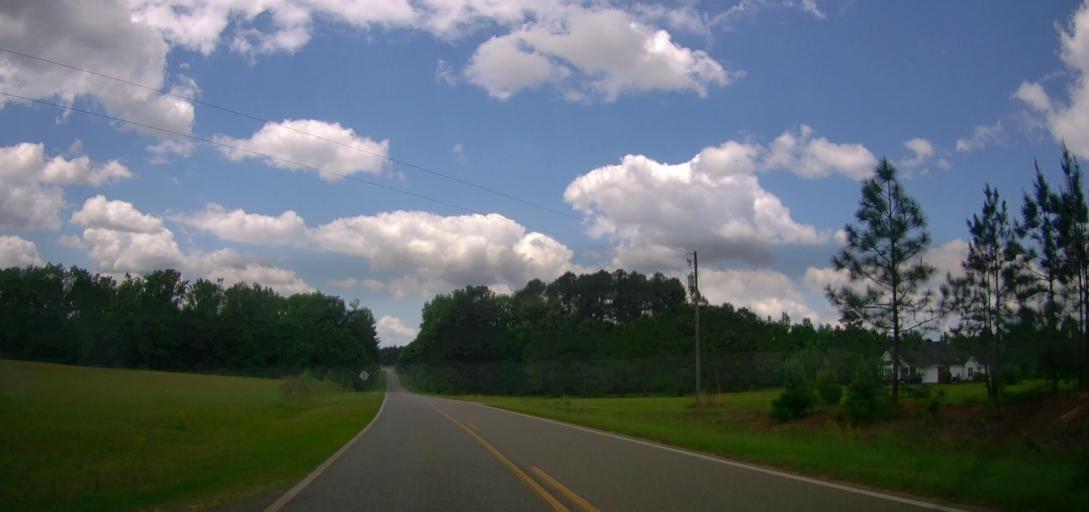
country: US
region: Georgia
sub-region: Laurens County
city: East Dublin
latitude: 32.6153
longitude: -82.8105
